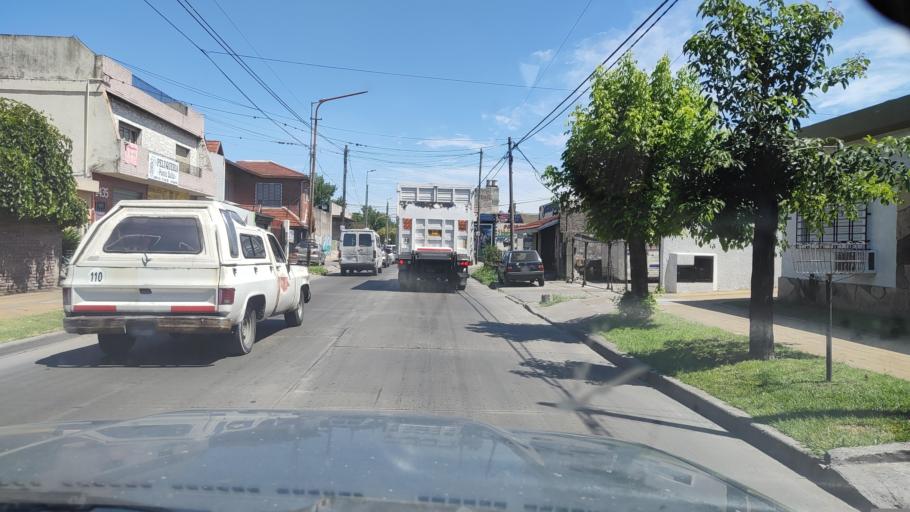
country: AR
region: Buenos Aires
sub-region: Partido de Moron
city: Moron
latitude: -34.6637
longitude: -58.6018
